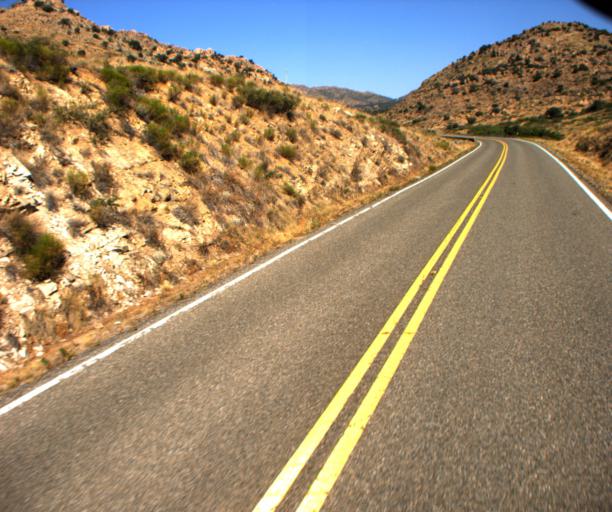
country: US
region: Arizona
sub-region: Graham County
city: Swift Trail Junction
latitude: 32.5610
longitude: -109.7893
